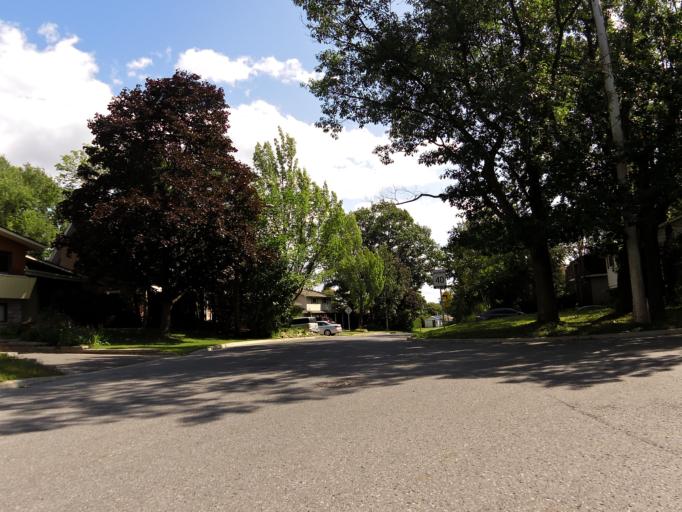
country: CA
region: Ontario
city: Bells Corners
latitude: 45.3552
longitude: -75.7920
